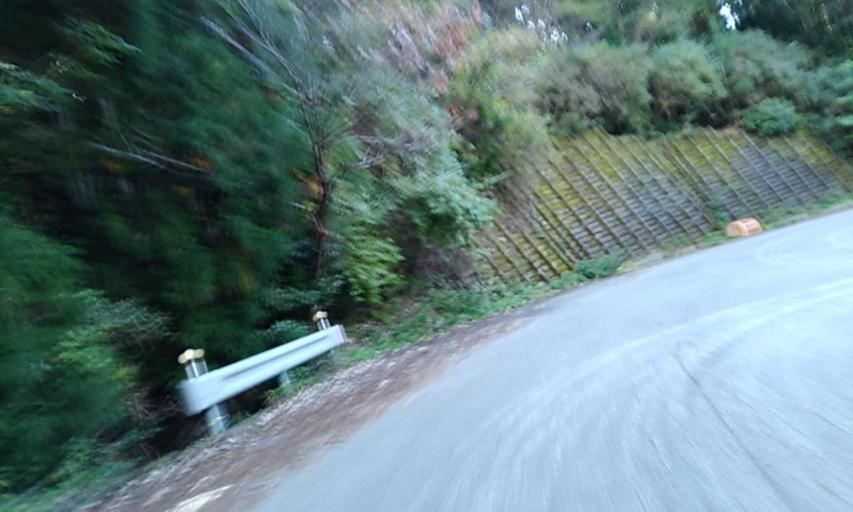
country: JP
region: Wakayama
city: Iwade
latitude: 34.1120
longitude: 135.3456
